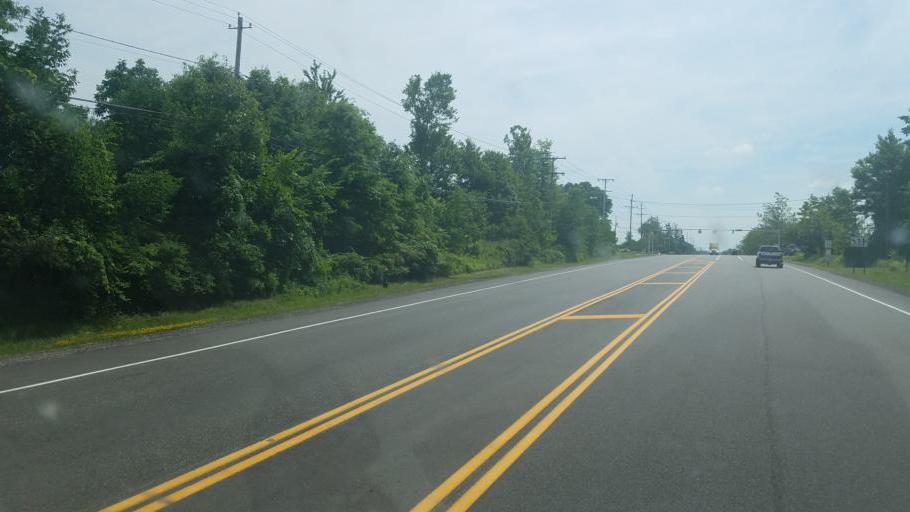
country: US
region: Ohio
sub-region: Summit County
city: Macedonia
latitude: 41.3114
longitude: -81.4746
